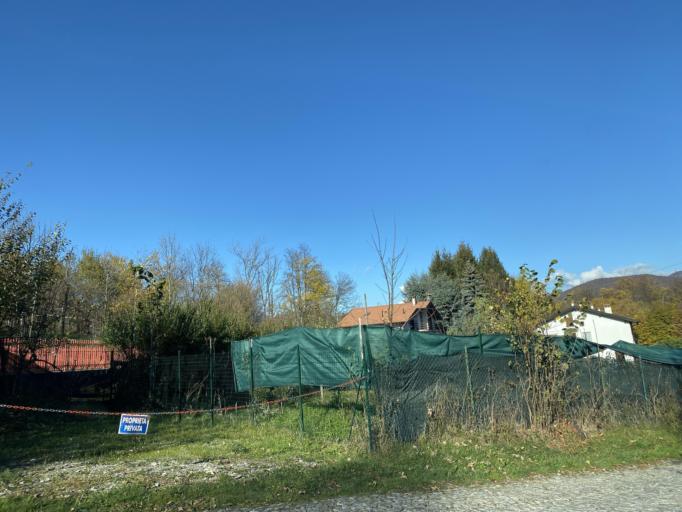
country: IT
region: Lombardy
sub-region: Provincia di Como
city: Pellio Intelvi
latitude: 45.9728
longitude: 9.0499
